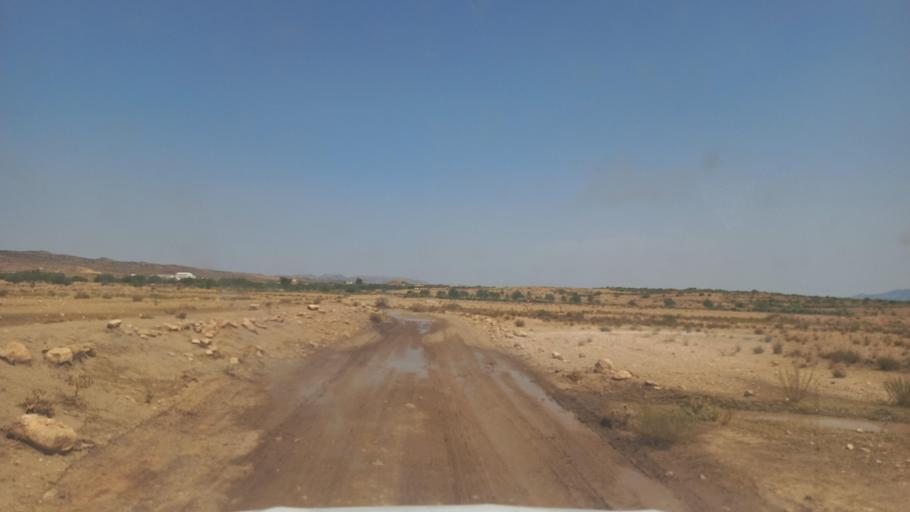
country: TN
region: Al Qasrayn
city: Kasserine
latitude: 35.2905
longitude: 8.9527
